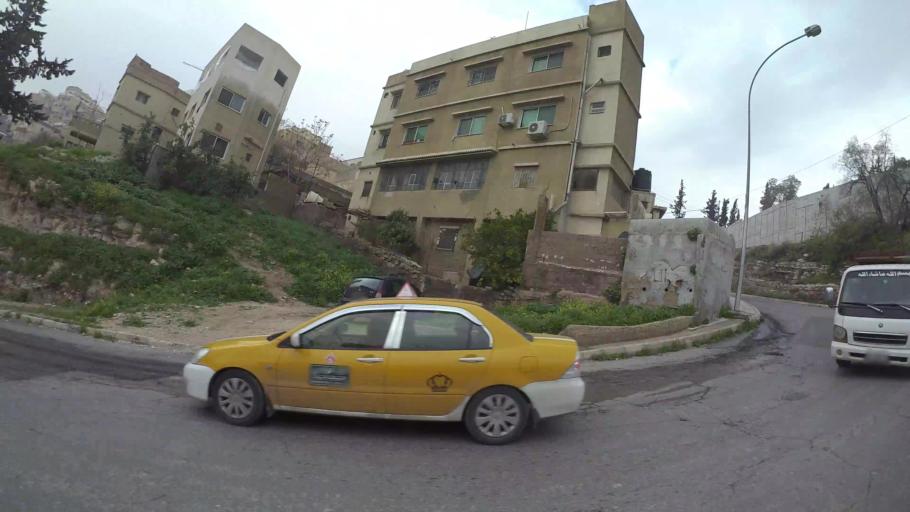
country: JO
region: Amman
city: Amman
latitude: 31.9561
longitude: 35.9443
